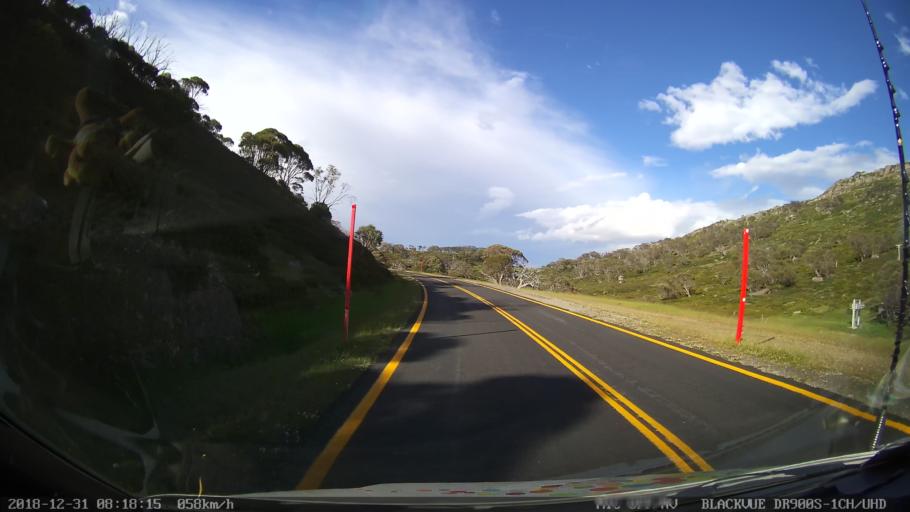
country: AU
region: New South Wales
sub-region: Snowy River
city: Jindabyne
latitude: -36.4132
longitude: 148.3968
